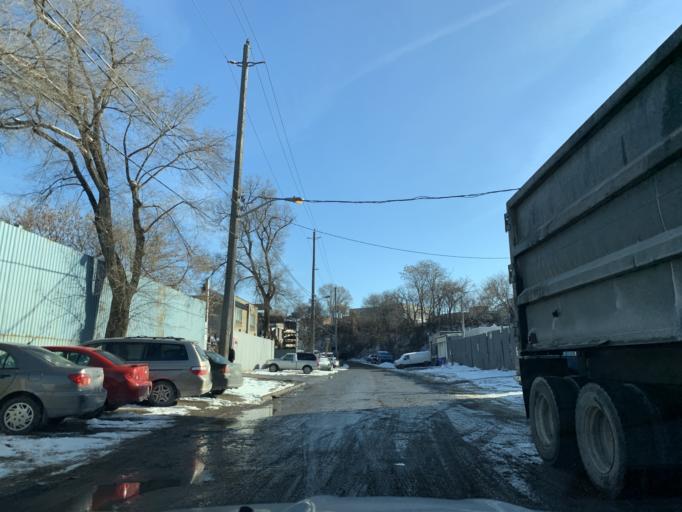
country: CA
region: Ontario
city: Toronto
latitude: 43.6839
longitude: -79.4780
